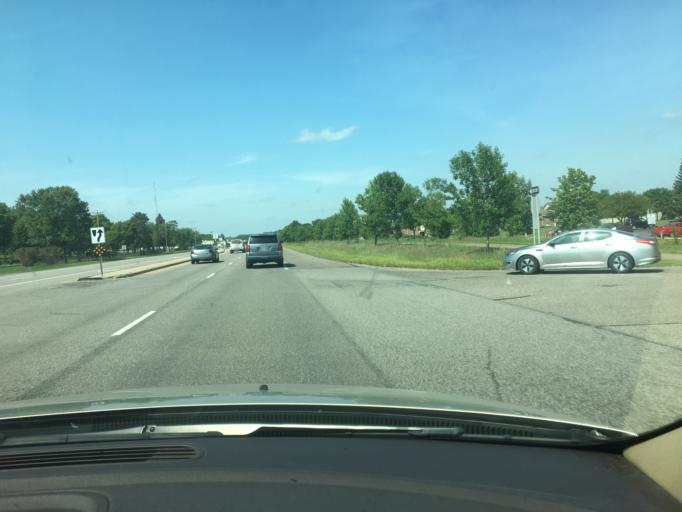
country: US
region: Minnesota
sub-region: Stearns County
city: Saint Cloud
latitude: 45.5286
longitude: -94.1631
